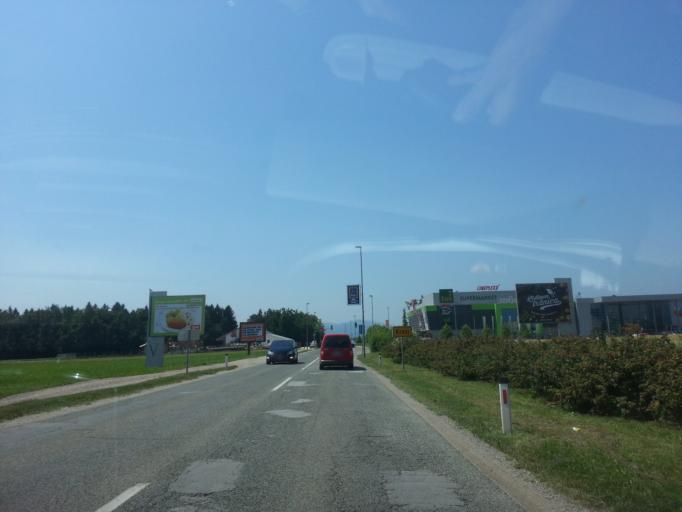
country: SI
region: Kranj
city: Kranj
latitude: 46.2380
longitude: 14.3765
